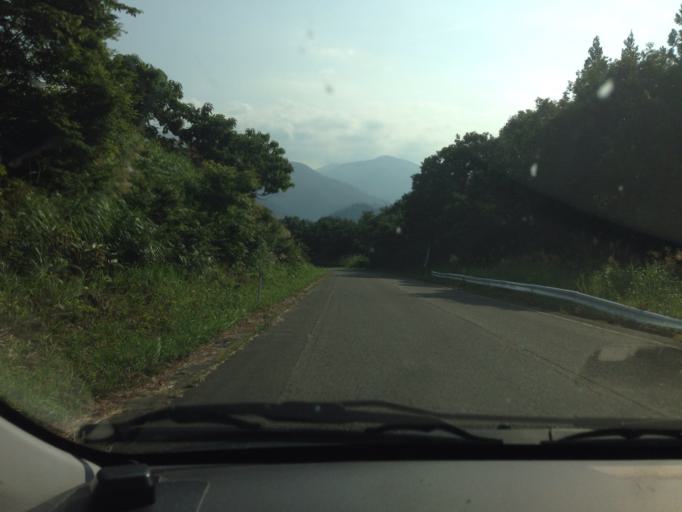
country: JP
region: Fukushima
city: Kitakata
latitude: 37.7455
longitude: 139.8684
